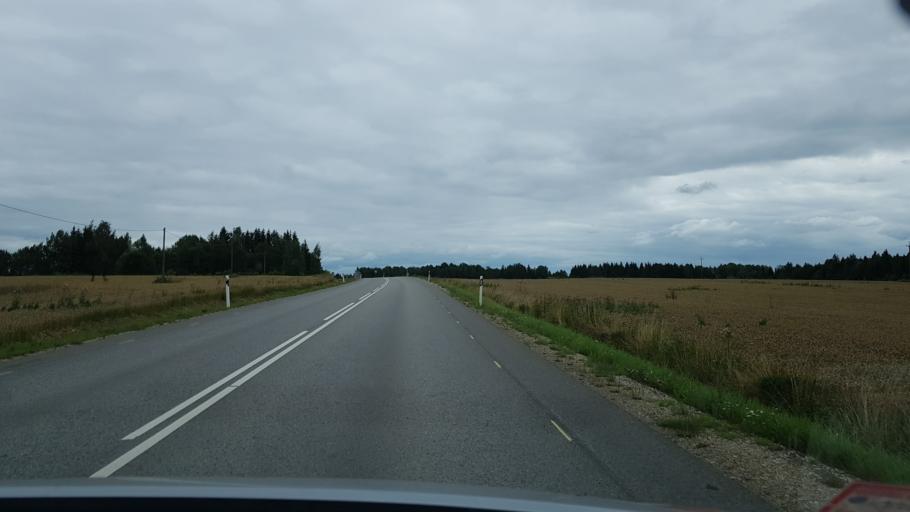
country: EE
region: Polvamaa
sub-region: Polva linn
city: Polva
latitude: 58.0597
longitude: 26.9136
